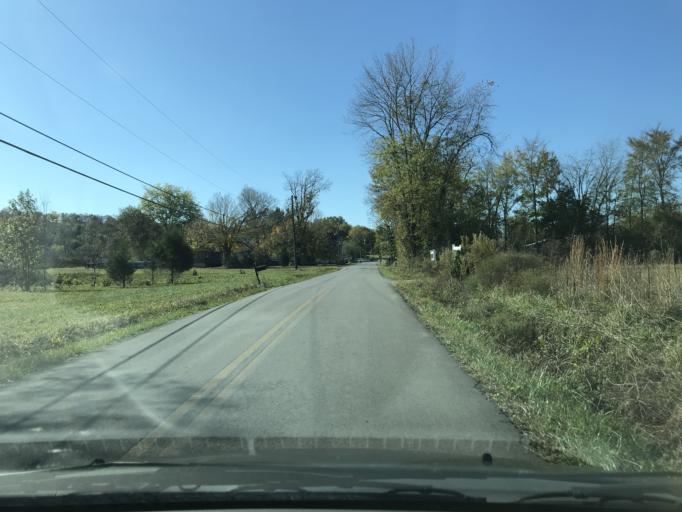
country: US
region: Georgia
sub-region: Dade County
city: Trenton
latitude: 34.9103
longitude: -85.4762
